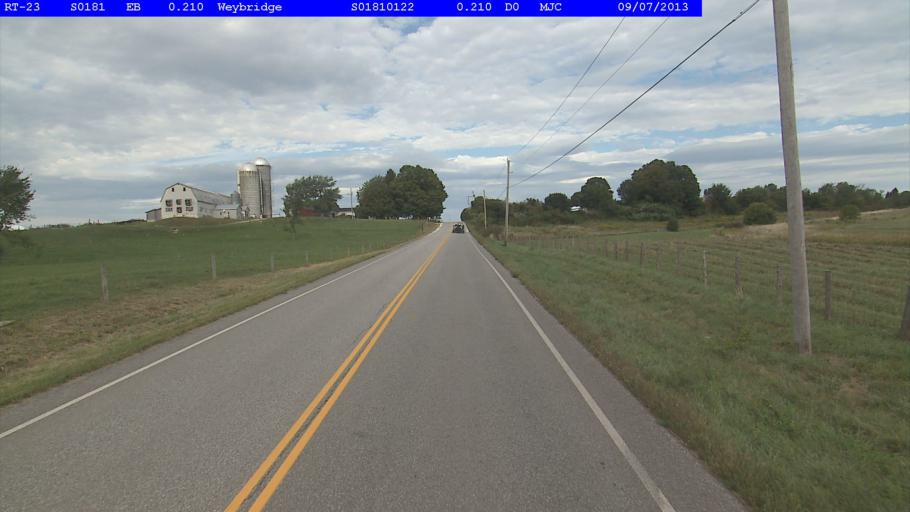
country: US
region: Vermont
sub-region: Addison County
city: Middlebury (village)
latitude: 44.0210
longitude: -73.1857
